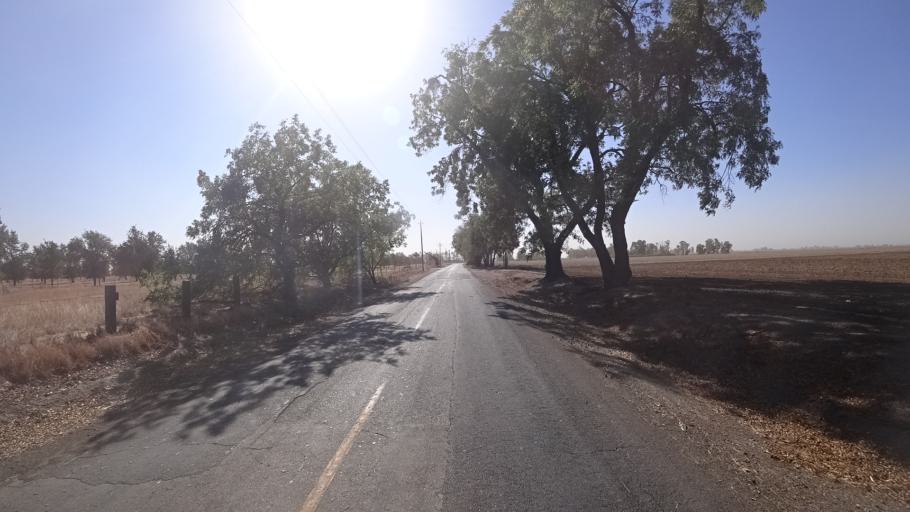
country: US
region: California
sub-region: Yolo County
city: Davis
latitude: 38.4921
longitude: -121.6956
